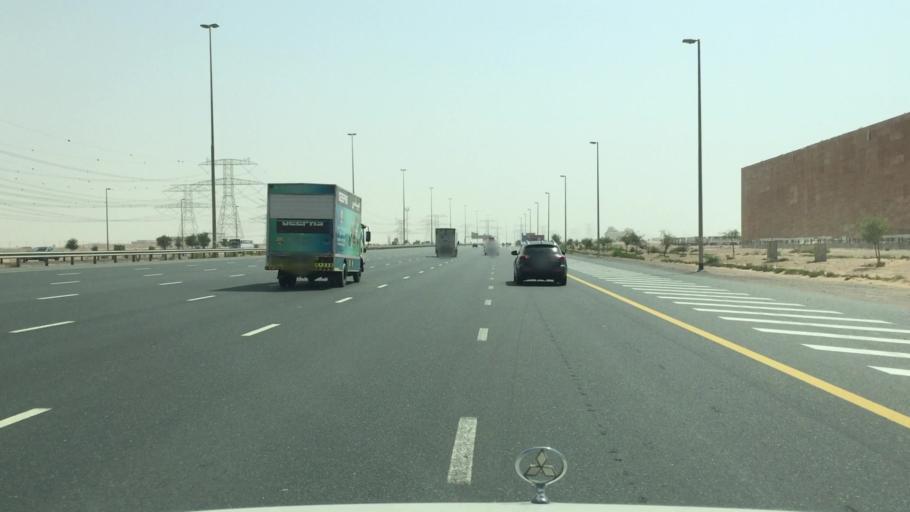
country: AE
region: Dubai
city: Dubai
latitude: 25.0815
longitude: 55.3832
